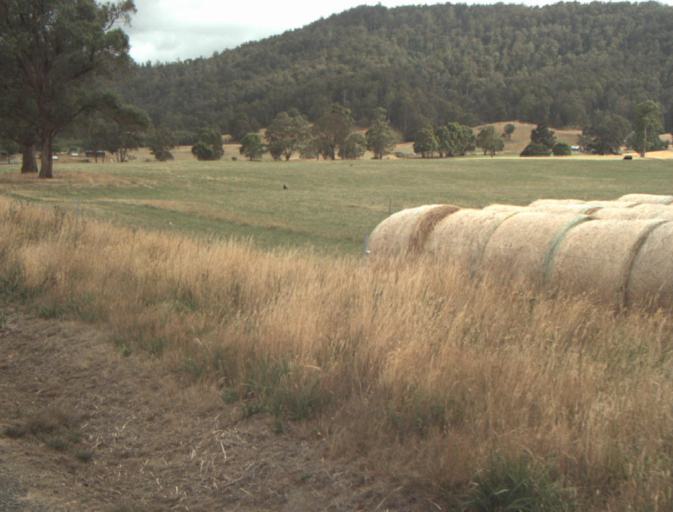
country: AU
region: Tasmania
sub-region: Dorset
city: Scottsdale
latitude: -41.4648
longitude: 147.5723
